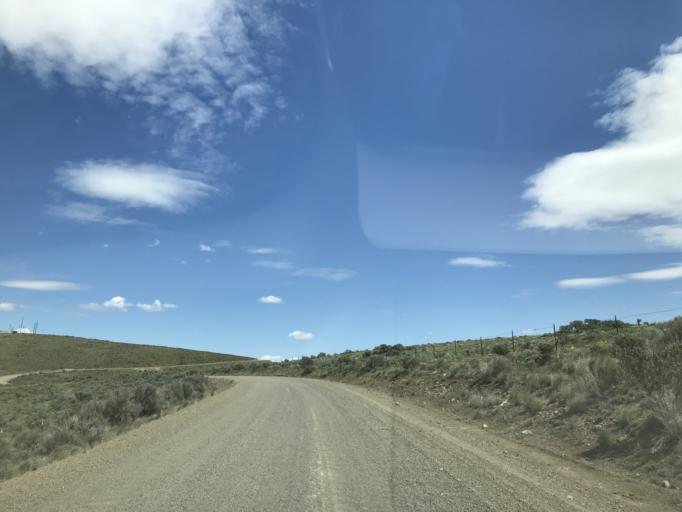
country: US
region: Washington
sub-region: Grant County
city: Quincy
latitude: 47.3172
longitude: -119.8096
